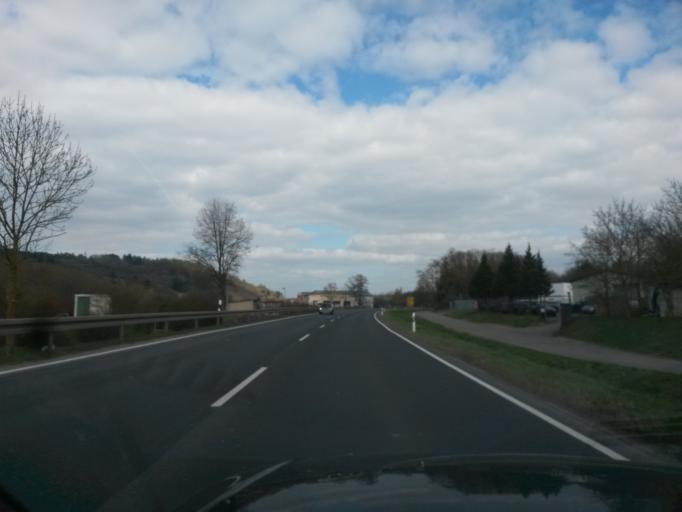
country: DE
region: Bavaria
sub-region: Regierungsbezirk Unterfranken
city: Eibelstadt
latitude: 49.7260
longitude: 9.9940
